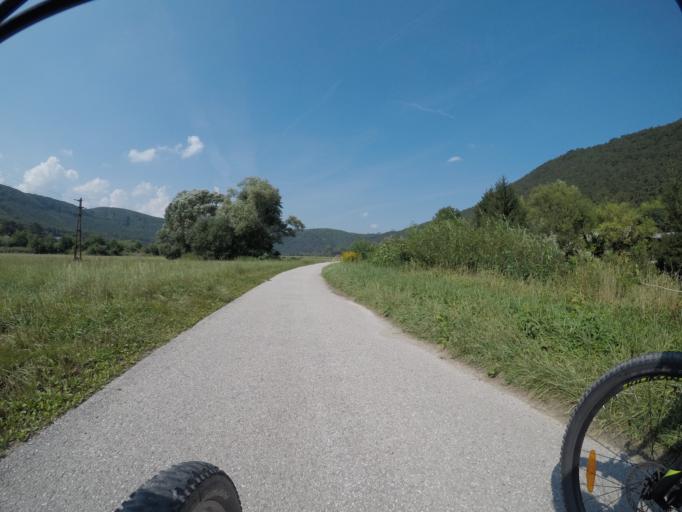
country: AT
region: Lower Austria
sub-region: Politischer Bezirk Baden
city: Pottenstein
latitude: 47.9727
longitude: 16.0710
